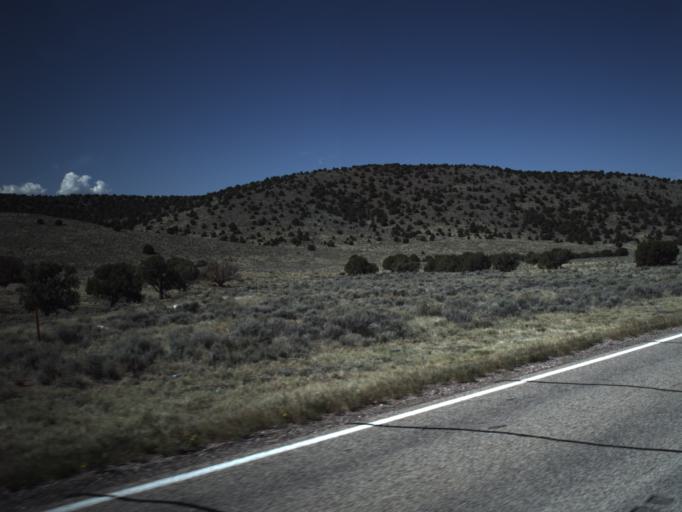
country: US
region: Utah
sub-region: Washington County
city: Enterprise
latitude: 37.6686
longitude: -113.4805
